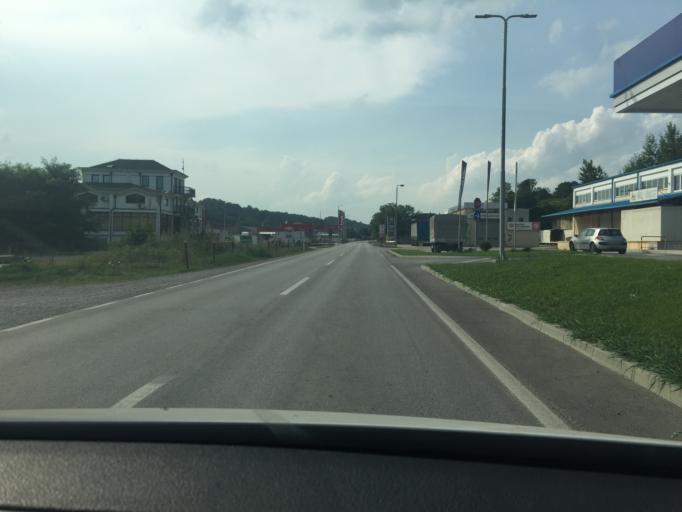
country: BA
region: Federation of Bosnia and Herzegovina
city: Mionica
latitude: 44.8231
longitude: 18.4565
